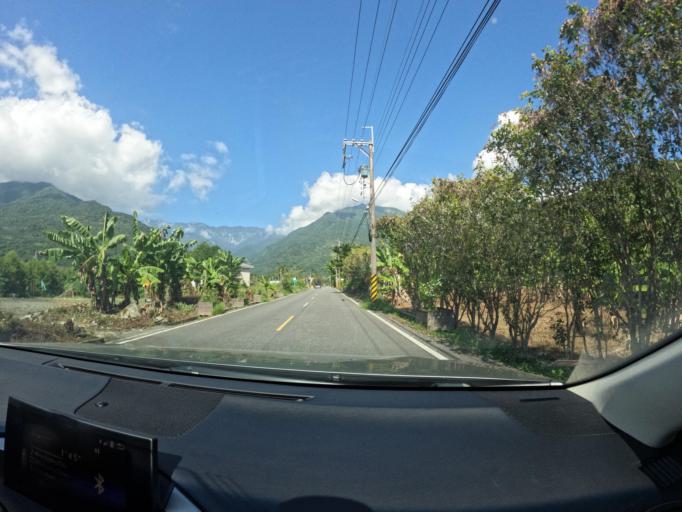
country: TW
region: Taiwan
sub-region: Hualien
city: Hualian
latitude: 23.5803
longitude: 121.3705
